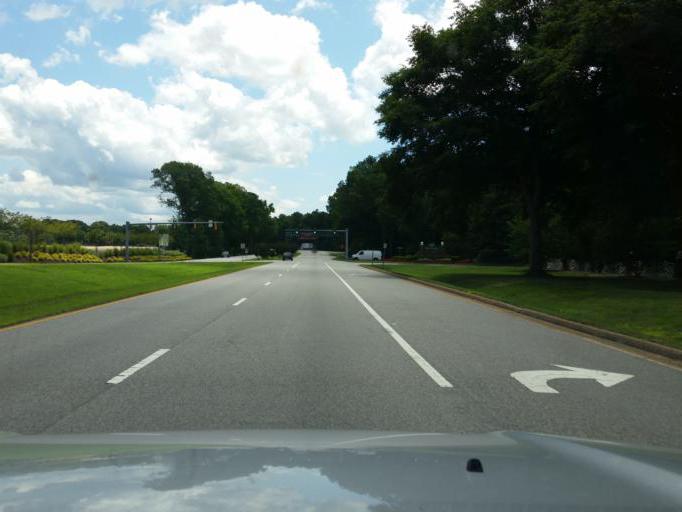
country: US
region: Virginia
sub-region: City of Williamsburg
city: Williamsburg
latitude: 37.2444
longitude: -76.6565
